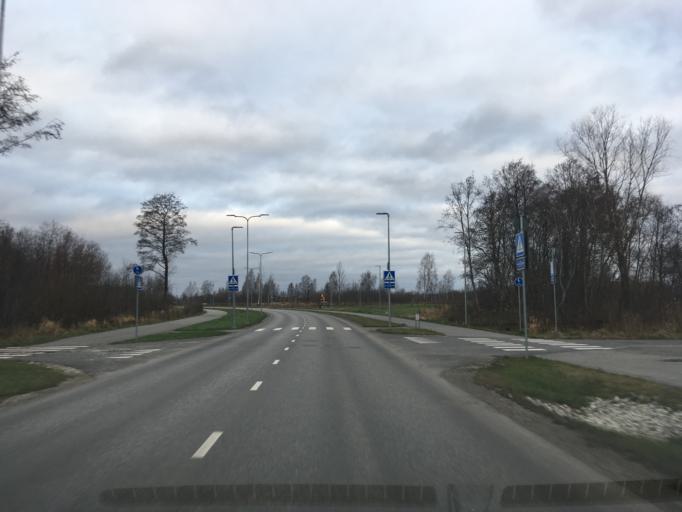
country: EE
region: Paernumaa
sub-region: Paernu linn
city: Parnu
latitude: 58.3997
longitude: 24.4807
